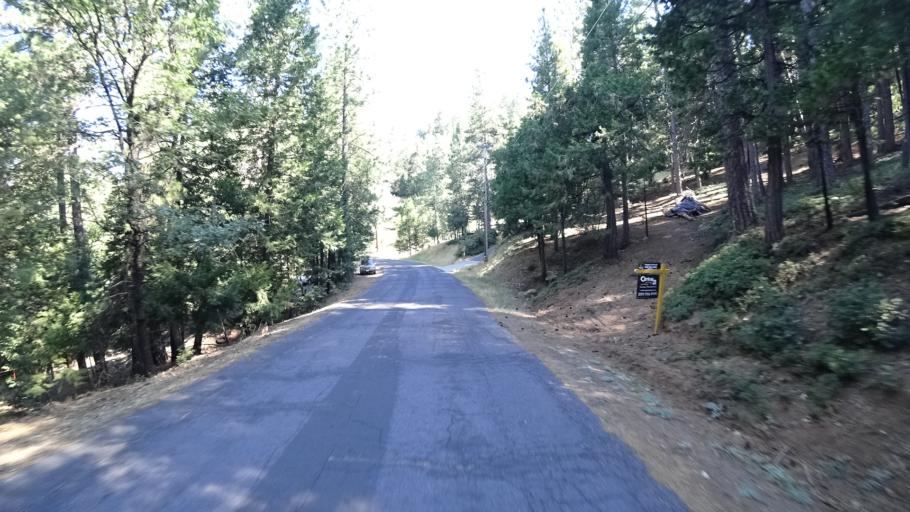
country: US
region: California
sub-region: Calaveras County
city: Arnold
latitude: 38.2448
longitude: -120.3692
